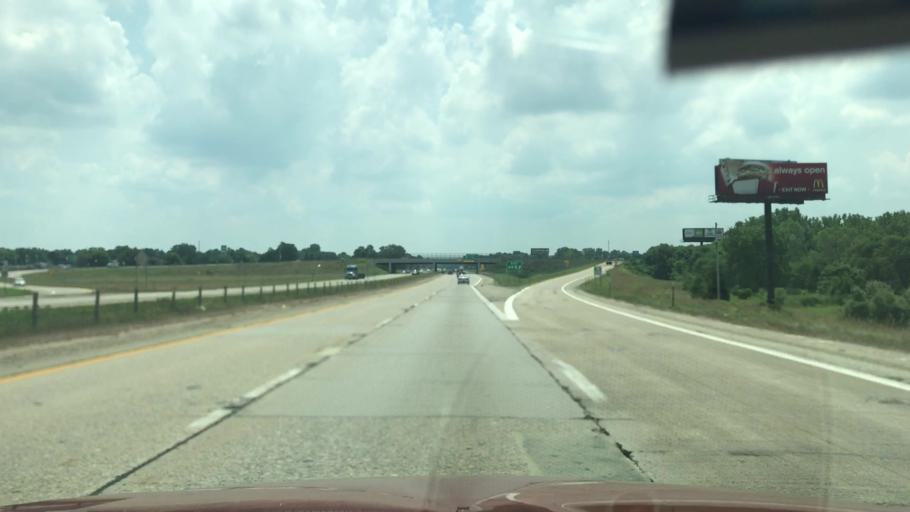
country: US
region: Michigan
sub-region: Allegan County
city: Plainwell
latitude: 42.4536
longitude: -85.6544
